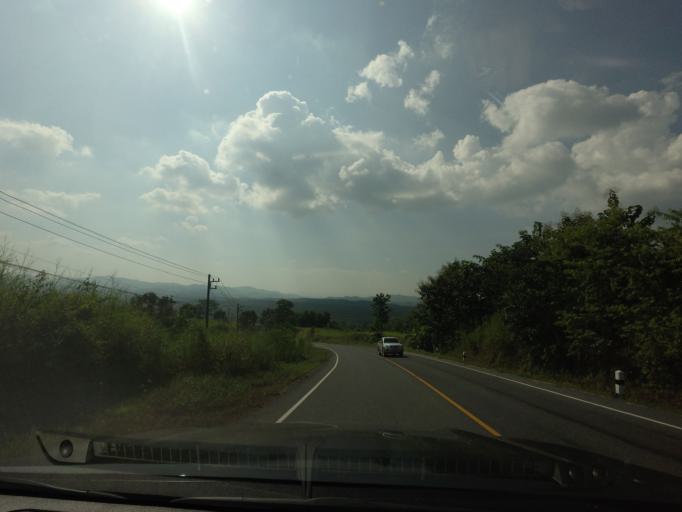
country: TH
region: Nan
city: Santi Suk
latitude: 18.9826
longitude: 100.9467
